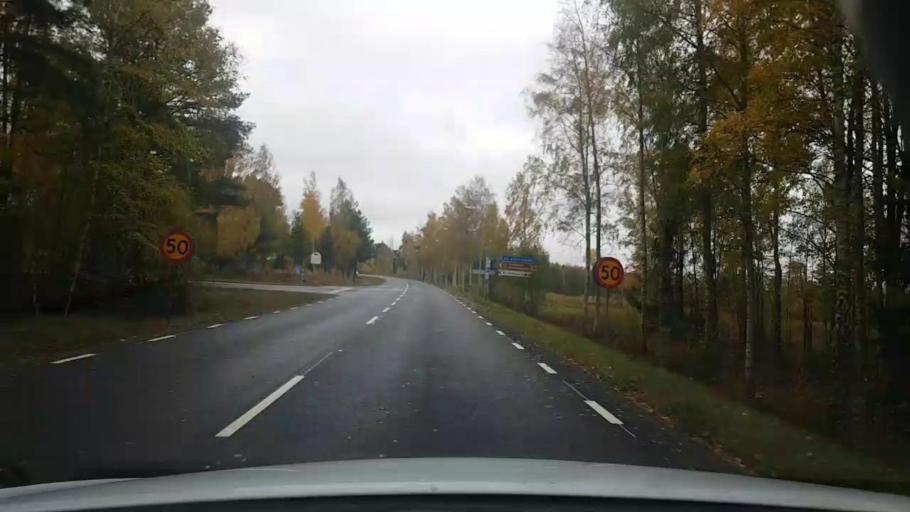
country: SE
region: OErebro
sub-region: Laxa Kommun
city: Laxa
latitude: 58.7813
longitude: 14.5360
